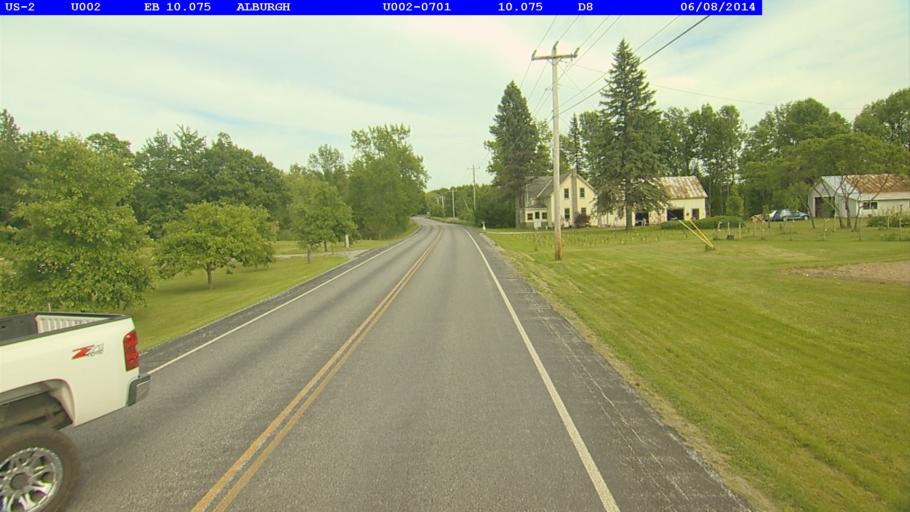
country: US
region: Vermont
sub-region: Grand Isle County
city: North Hero
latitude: 44.9061
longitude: -73.2782
